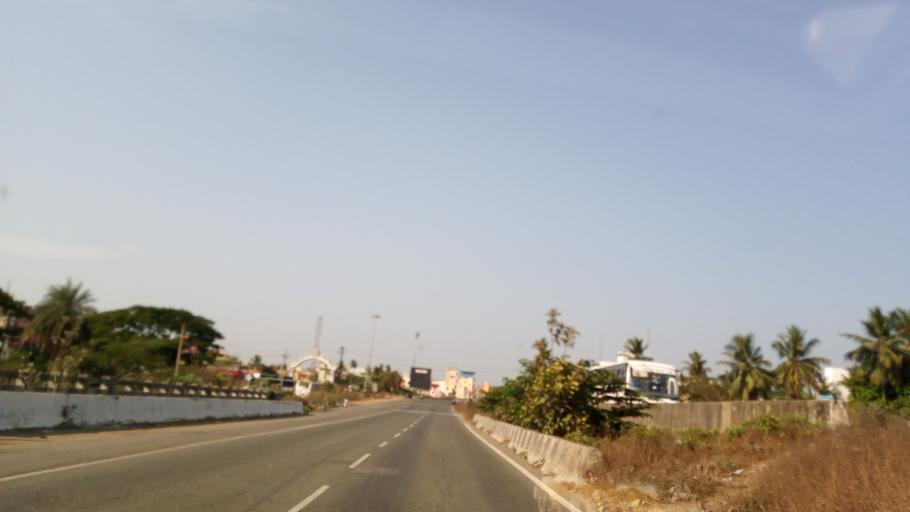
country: IN
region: Tamil Nadu
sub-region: Kancheepuram
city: Sriperumbudur
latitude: 12.9737
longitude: 79.9564
